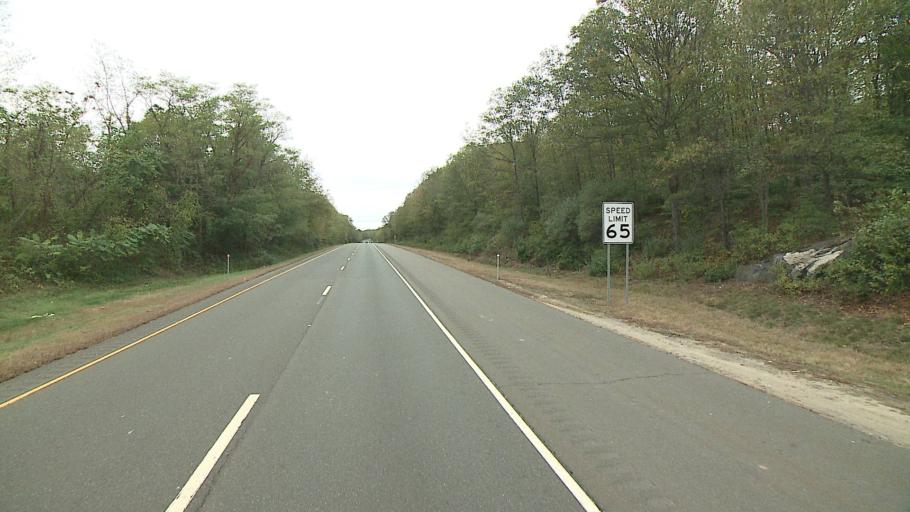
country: US
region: Connecticut
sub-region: Middlesex County
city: Essex Village
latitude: 41.3286
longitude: -72.3870
